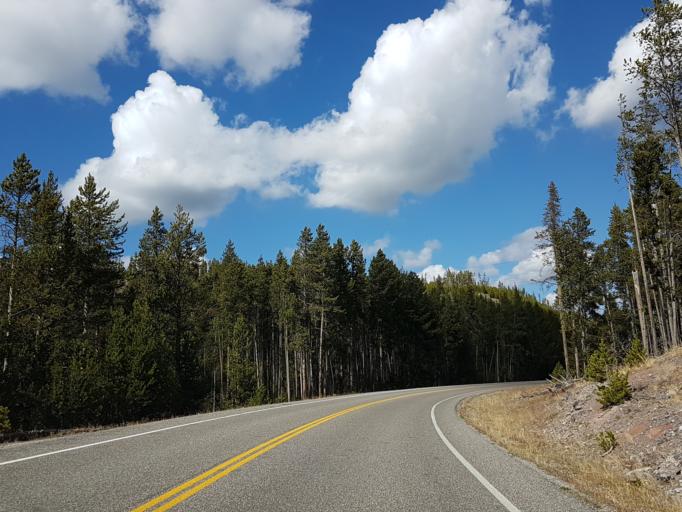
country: US
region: Montana
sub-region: Gallatin County
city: West Yellowstone
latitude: 44.5796
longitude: -110.8305
